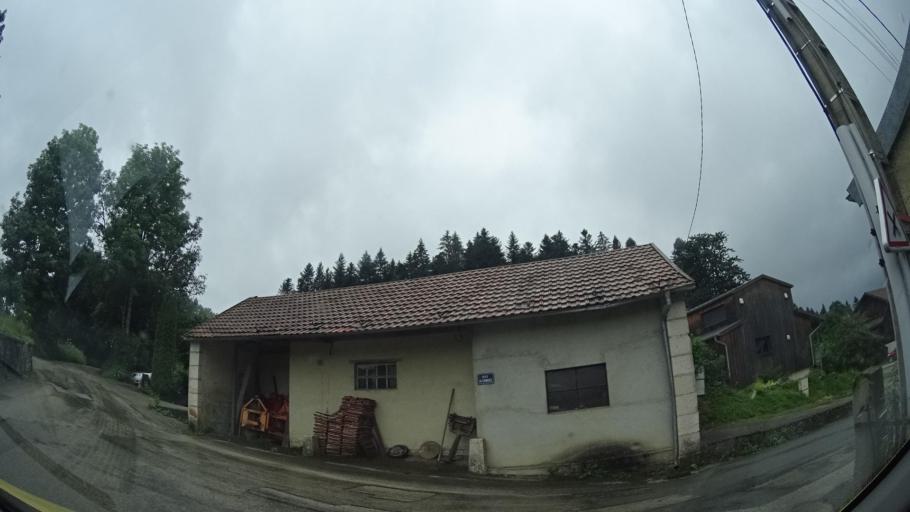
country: FR
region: Franche-Comte
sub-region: Departement du Doubs
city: Les Fourgs
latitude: 46.8244
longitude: 6.3424
